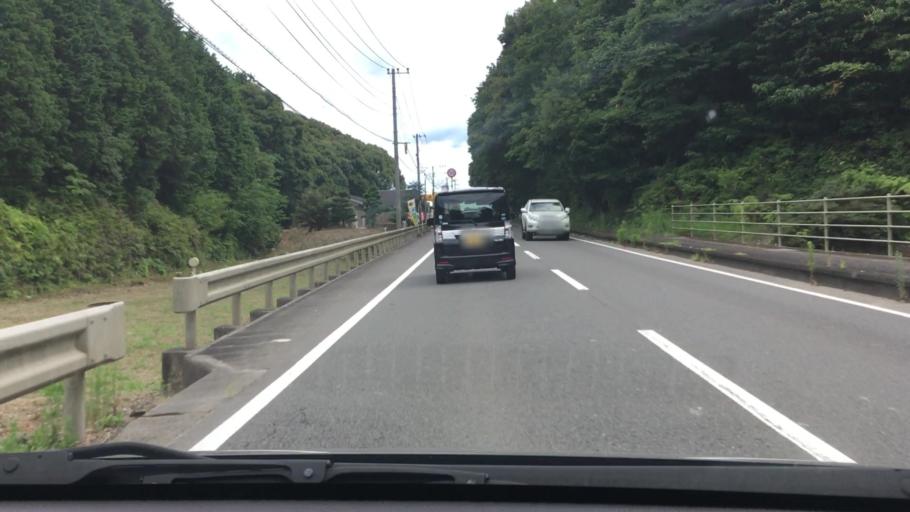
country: JP
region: Nagasaki
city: Togitsu
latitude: 32.9725
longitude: 129.7819
